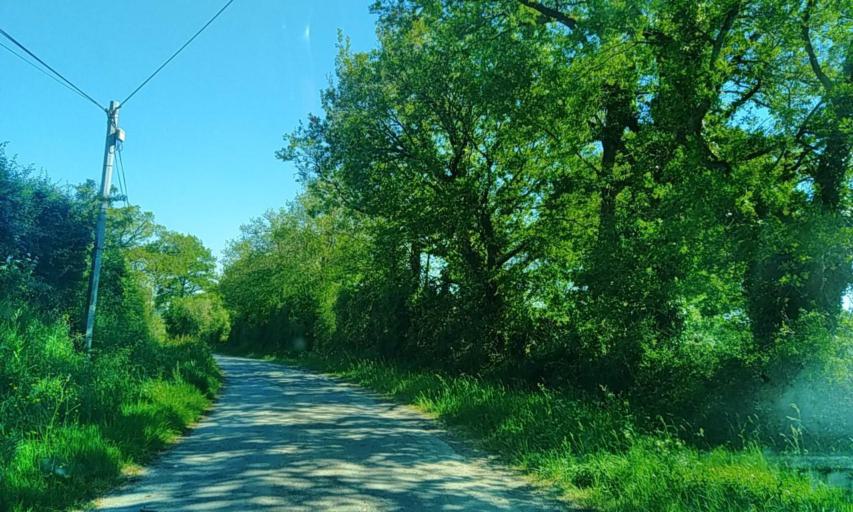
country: FR
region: Poitou-Charentes
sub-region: Departement des Deux-Sevres
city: Boisme
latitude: 46.7918
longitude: -0.4647
